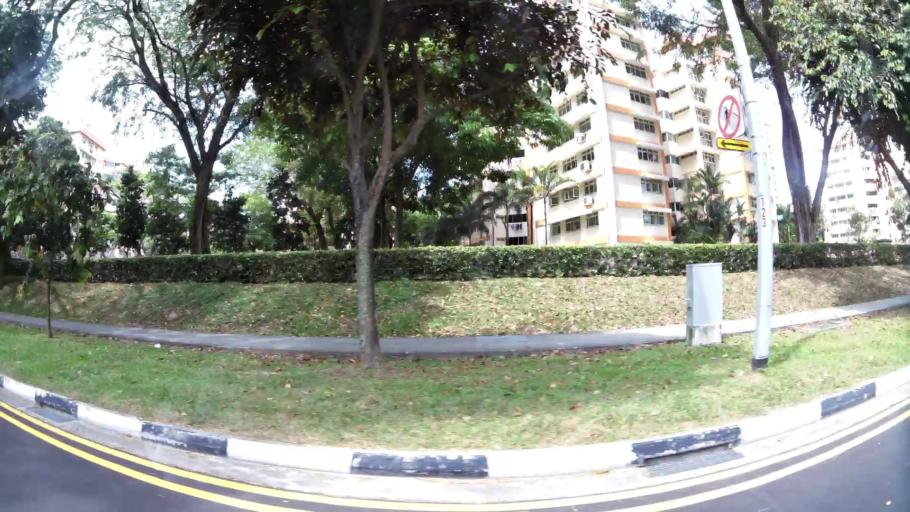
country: MY
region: Johor
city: Johor Bahru
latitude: 1.3439
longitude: 103.7161
